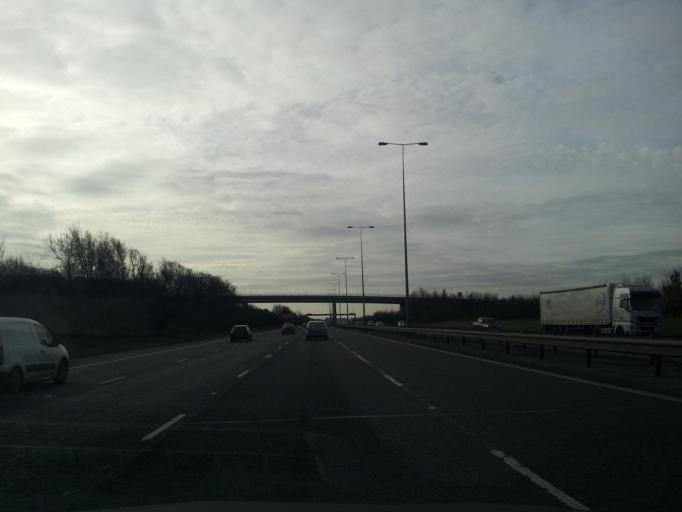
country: GB
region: England
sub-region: Cambridgeshire
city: Stilton
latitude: 52.4692
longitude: -0.2836
